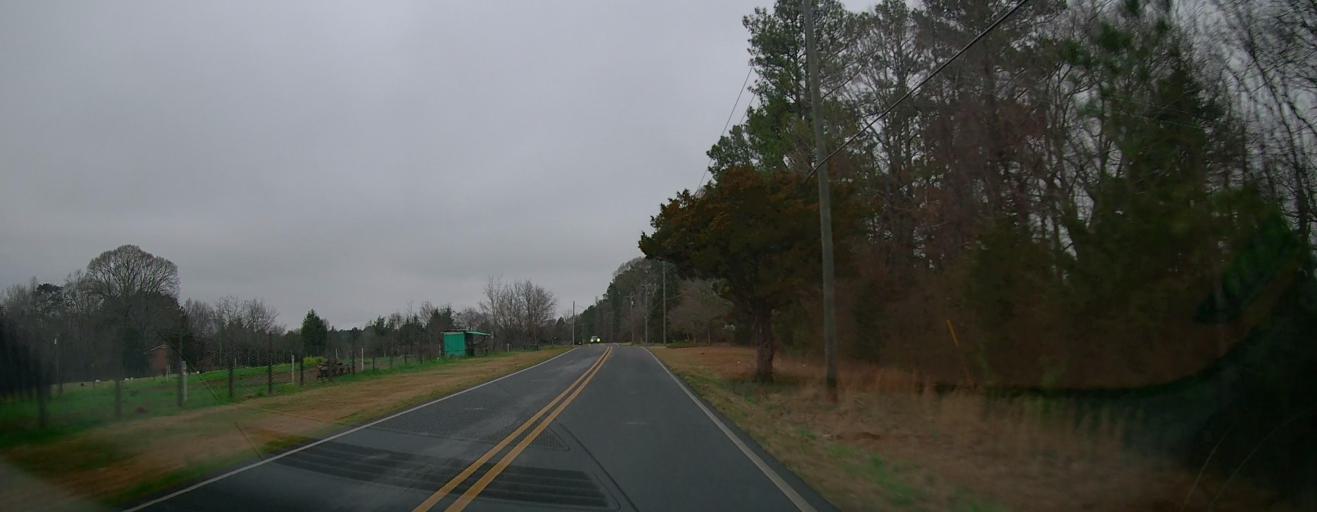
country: US
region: Georgia
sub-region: Pike County
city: Zebulon
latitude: 33.1417
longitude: -84.3459
